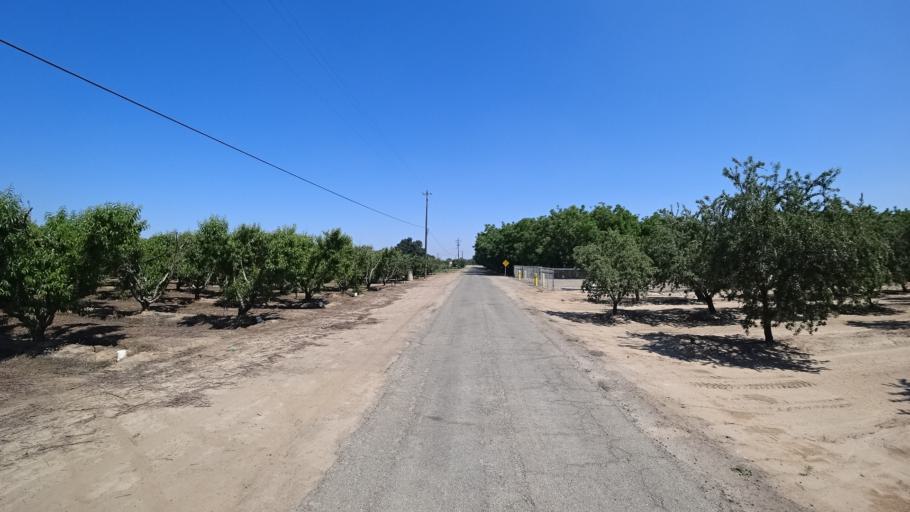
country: US
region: California
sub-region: Fresno County
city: Laton
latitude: 36.4487
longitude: -119.6184
